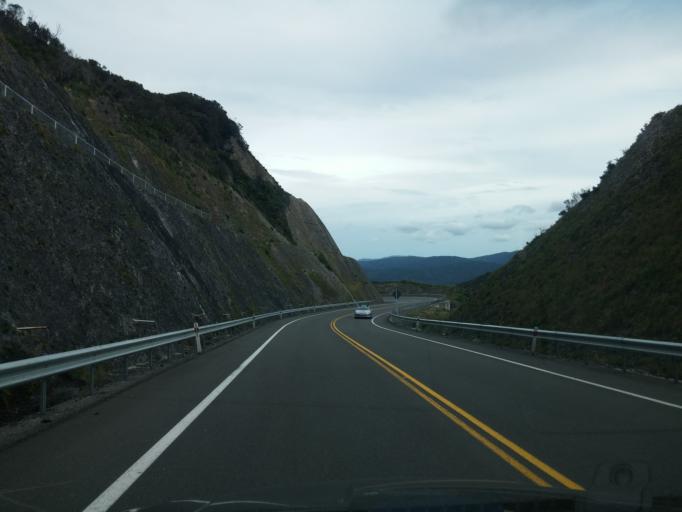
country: NZ
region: Wellington
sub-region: Upper Hutt City
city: Upper Hutt
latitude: -41.1155
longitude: 175.2288
